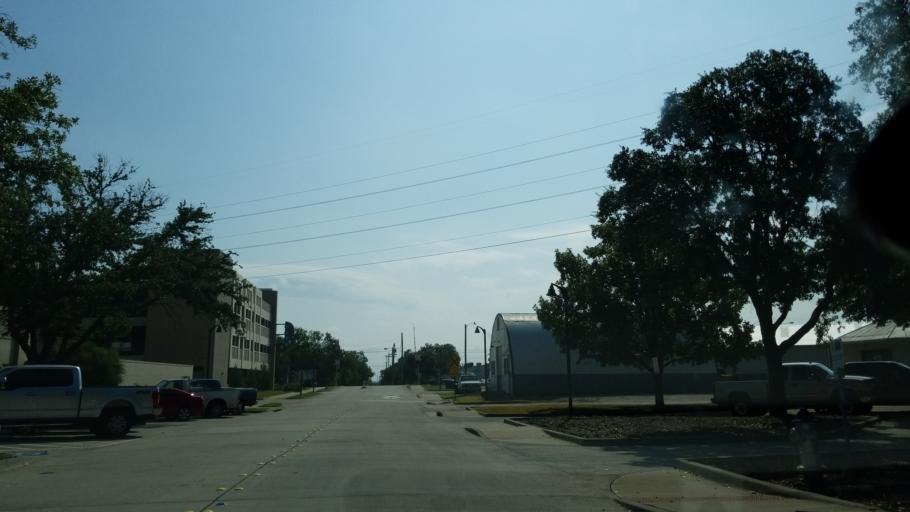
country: US
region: Texas
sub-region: Dallas County
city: Garland
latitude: 32.9134
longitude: -96.6365
